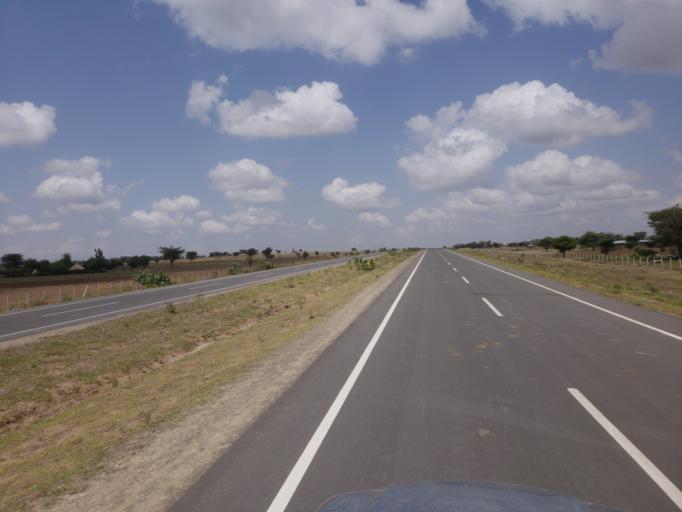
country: ET
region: Oromiya
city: Mojo
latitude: 8.3236
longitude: 38.9569
